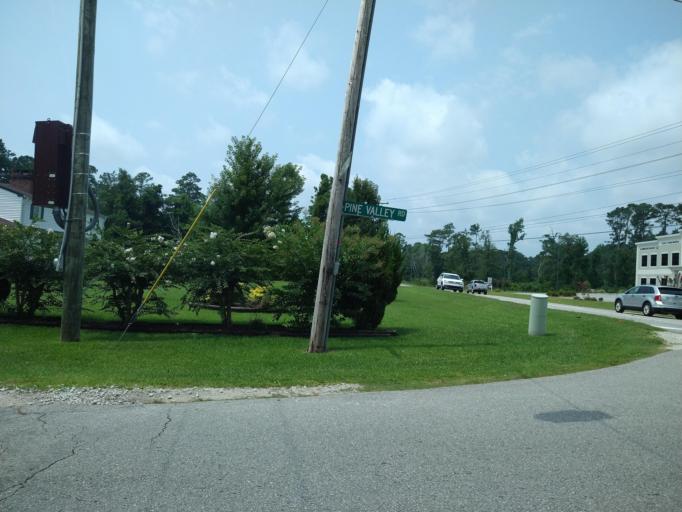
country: US
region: North Carolina
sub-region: Onslow County
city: Pumpkin Center
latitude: 34.7698
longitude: -77.3734
